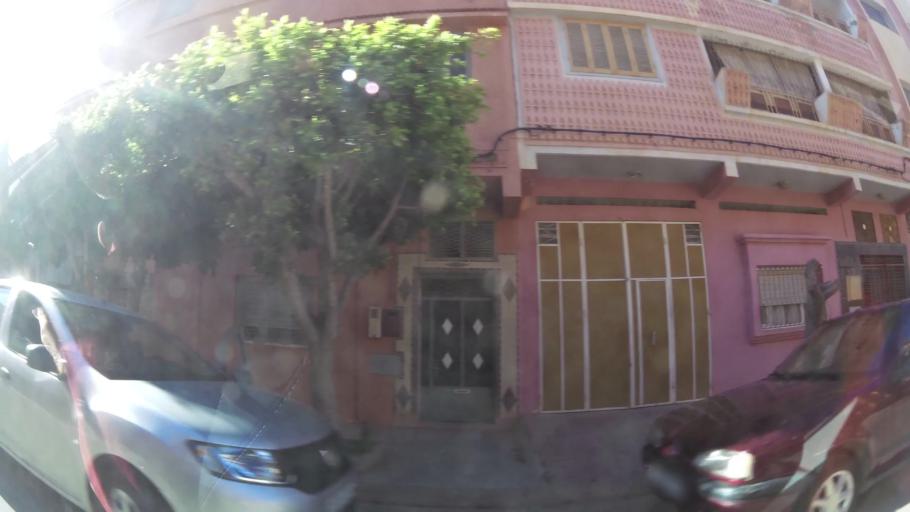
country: MA
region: Oriental
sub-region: Berkane-Taourirt
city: Berkane
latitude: 34.9313
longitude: -2.3320
